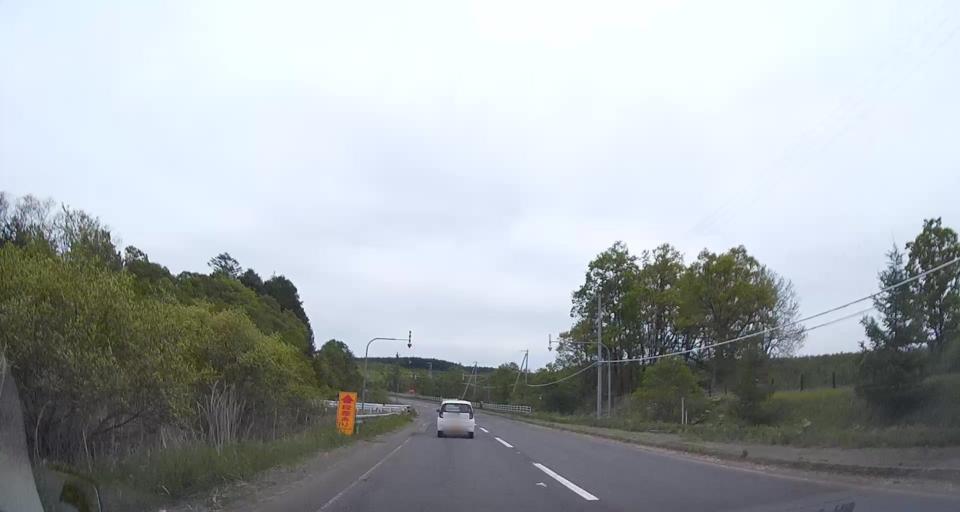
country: JP
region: Hokkaido
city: Chitose
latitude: 42.7691
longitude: 141.8381
